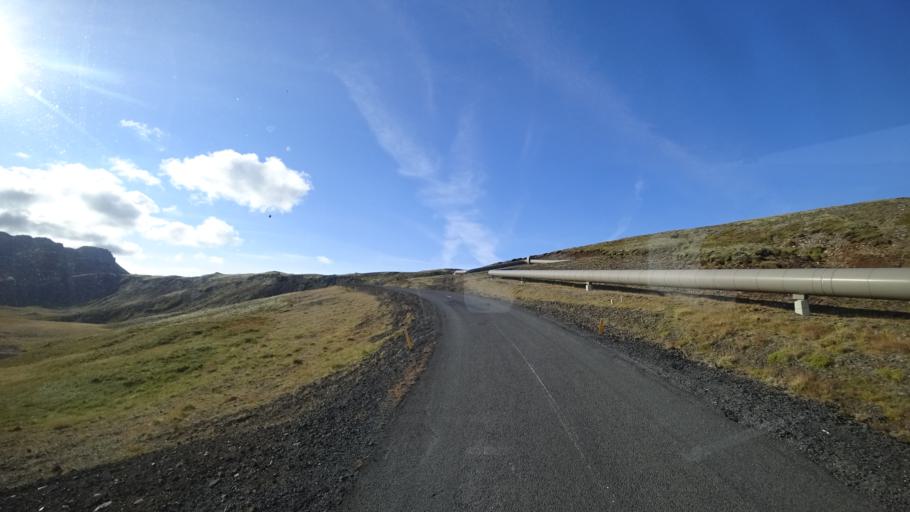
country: IS
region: South
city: Hveragerdi
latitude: 64.1074
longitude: -21.2754
